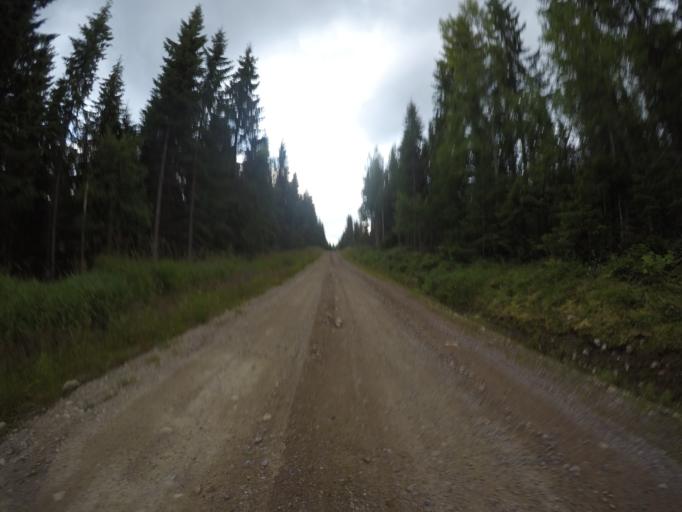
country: SE
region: Vaermland
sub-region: Filipstads Kommun
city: Lesjofors
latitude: 60.1991
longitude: 14.3790
